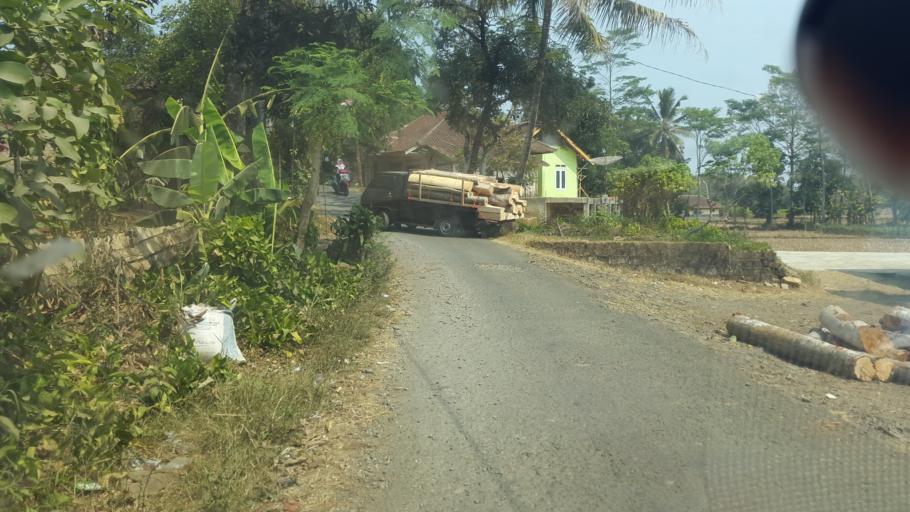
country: ID
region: West Java
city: Tegalloa
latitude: -7.2788
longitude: 106.6384
